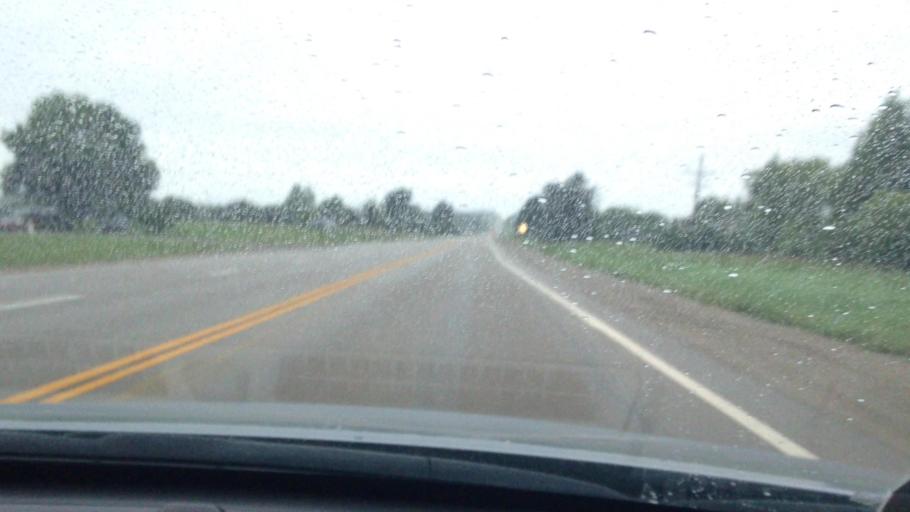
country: US
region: Kansas
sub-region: Brown County
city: Hiawatha
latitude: 39.8379
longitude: -95.5271
